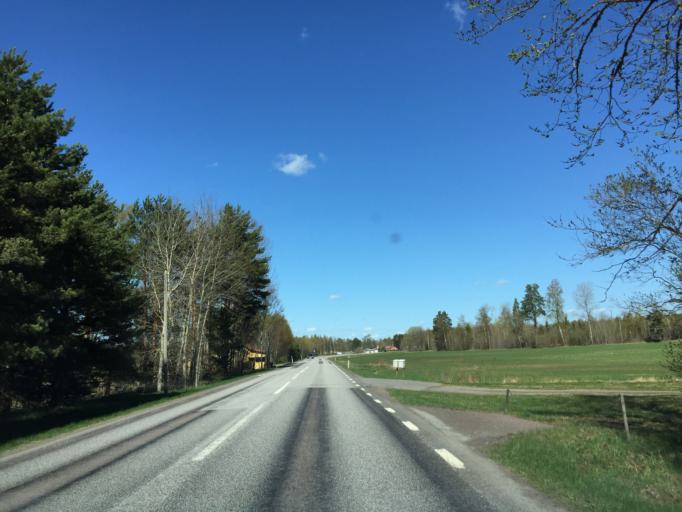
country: SE
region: OErebro
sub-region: Hallsbergs Kommun
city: Palsboda
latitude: 59.0959
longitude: 15.3240
